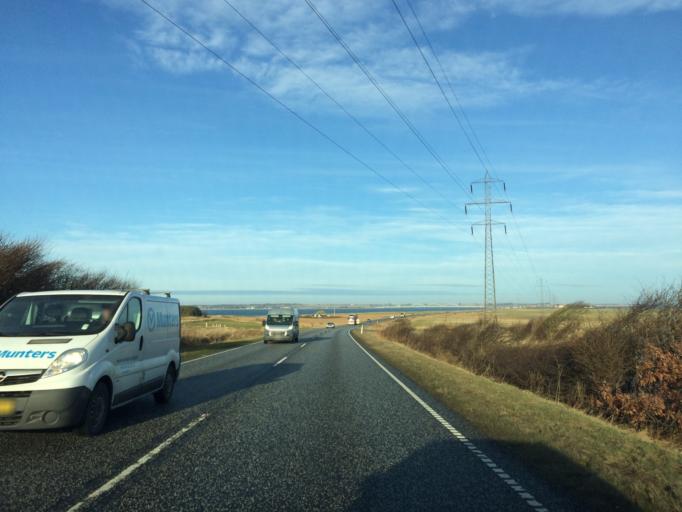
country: DK
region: Central Jutland
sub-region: Struer Kommune
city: Struer
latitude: 56.5570
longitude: 8.5575
